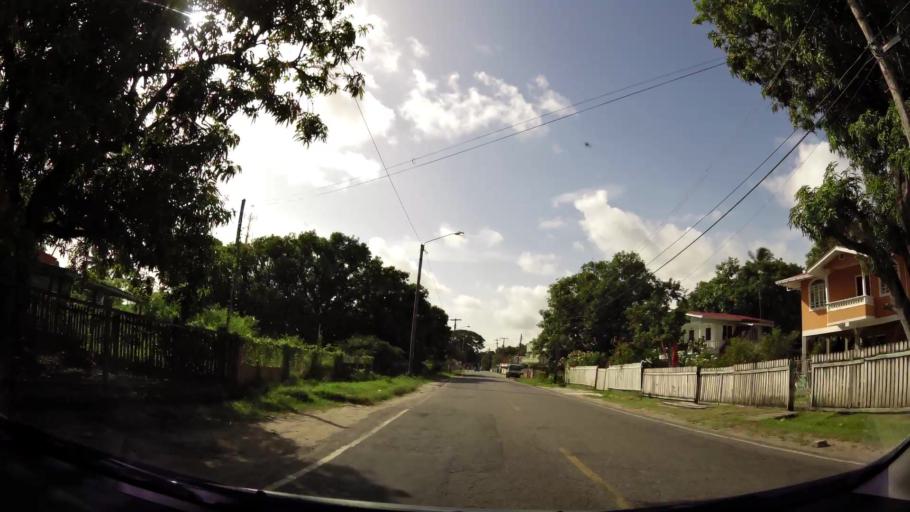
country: GY
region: Demerara-Mahaica
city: Mahaica Village
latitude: 6.7539
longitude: -57.9751
